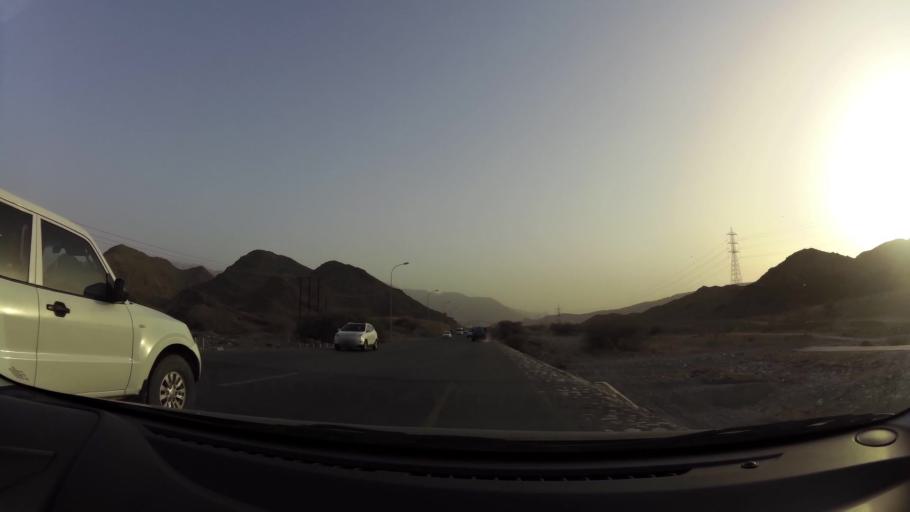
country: OM
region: Muhafazat Masqat
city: Bawshar
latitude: 23.4985
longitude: 58.3270
